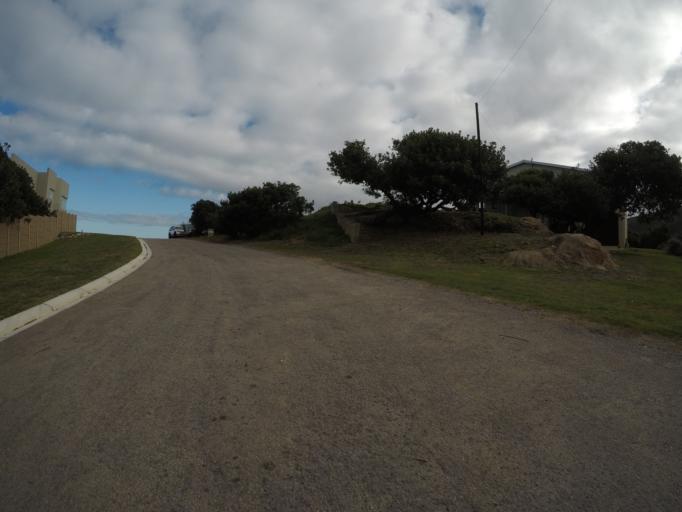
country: ZA
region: Western Cape
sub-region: Eden District Municipality
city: Riversdale
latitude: -34.4307
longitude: 21.3248
